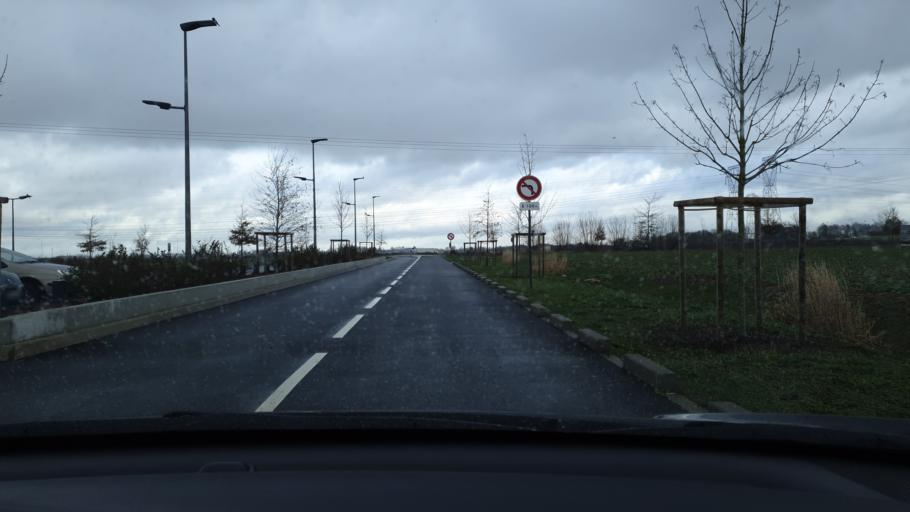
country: FR
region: Ile-de-France
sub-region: Departement de Seine-et-Marne
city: Mitry-Mory
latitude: 48.9640
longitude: 2.6005
